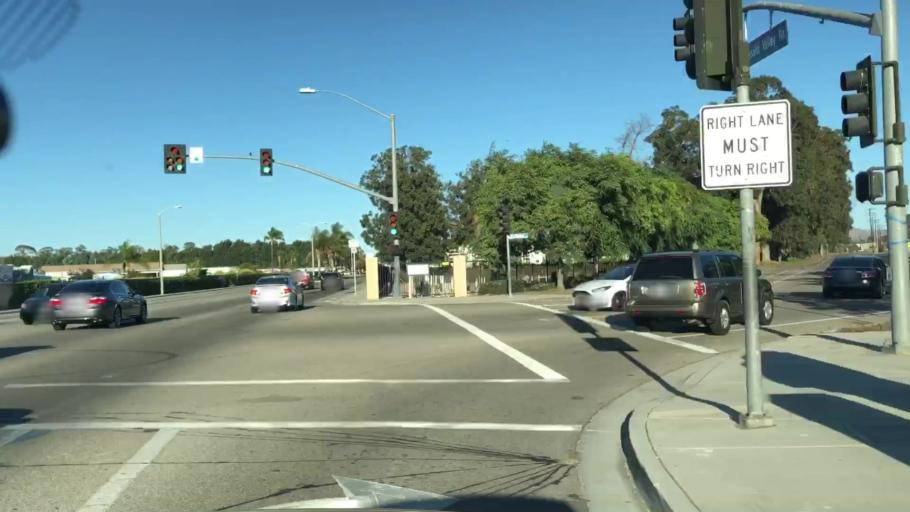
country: US
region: California
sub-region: Ventura County
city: Oxnard
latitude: 34.1617
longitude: -119.1516
